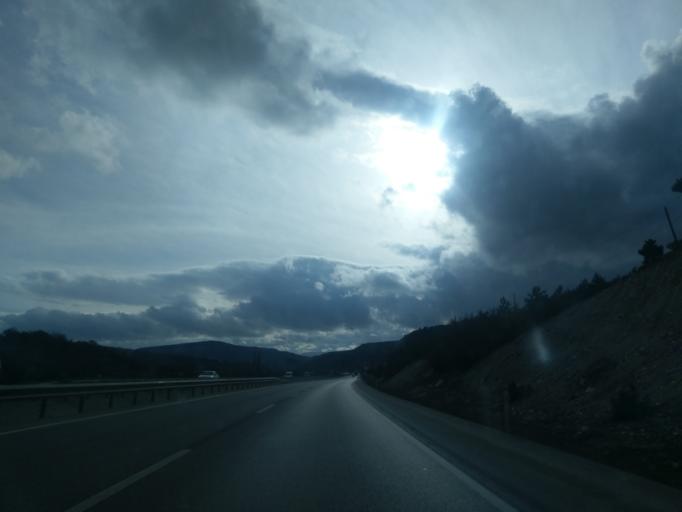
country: TR
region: Kuetahya
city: Sabuncu
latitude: 39.5480
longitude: 30.0594
